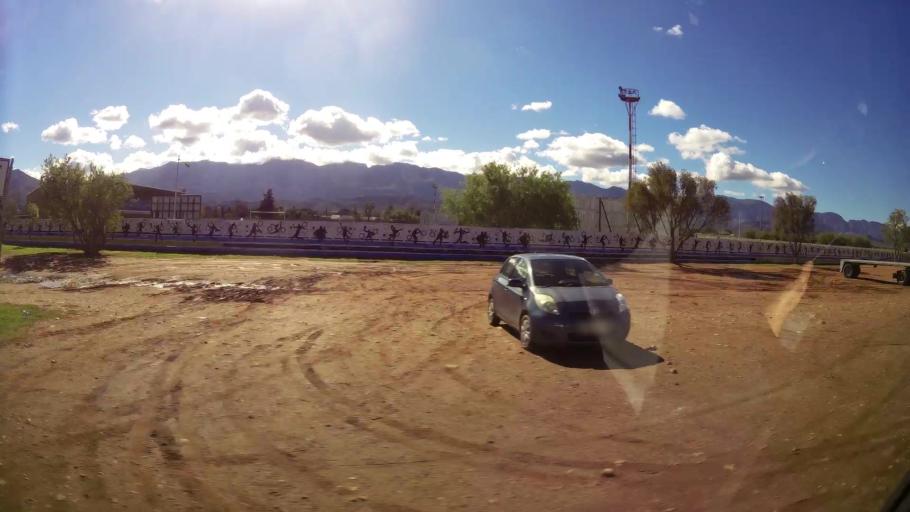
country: ZA
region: Western Cape
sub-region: Cape Winelands District Municipality
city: Ashton
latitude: -33.8137
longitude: 19.8943
